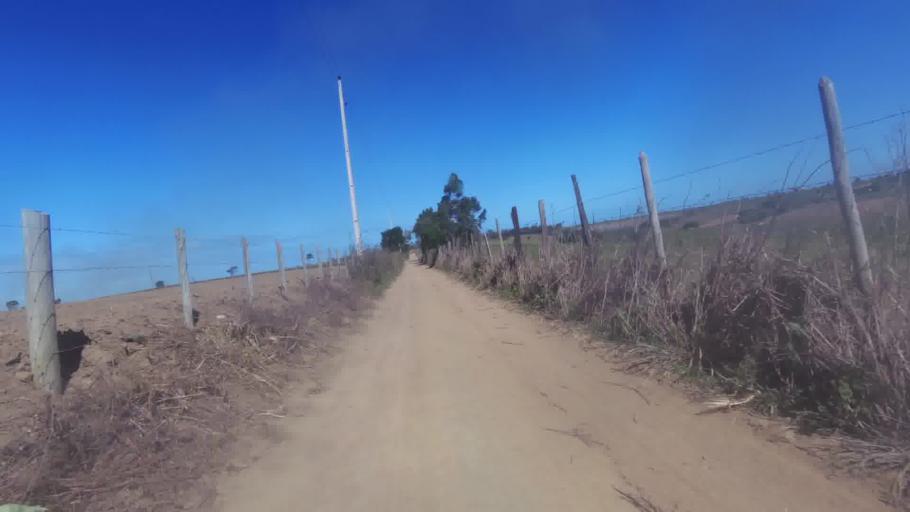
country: BR
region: Espirito Santo
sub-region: Marataizes
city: Marataizes
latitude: -21.1567
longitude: -40.9657
